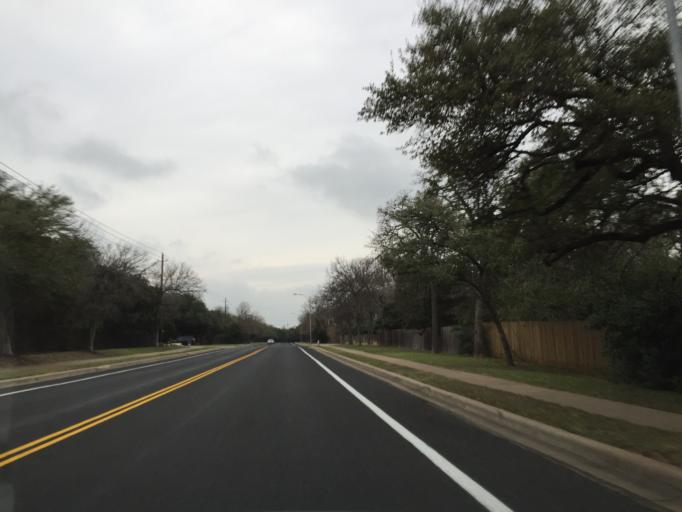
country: US
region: Texas
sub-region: Travis County
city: Barton Creek
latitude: 30.2462
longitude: -97.8391
